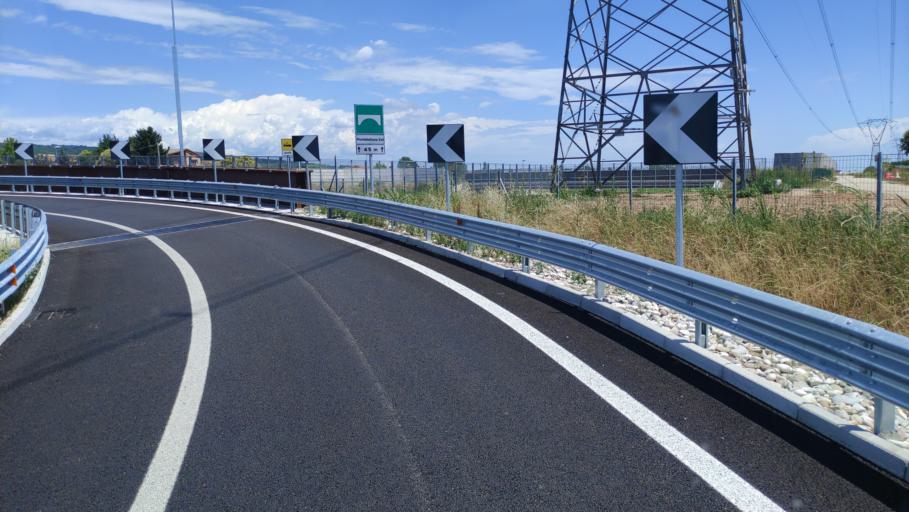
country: IT
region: Veneto
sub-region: Provincia di Treviso
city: Falze-Signoressa
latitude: 45.7614
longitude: 12.0959
